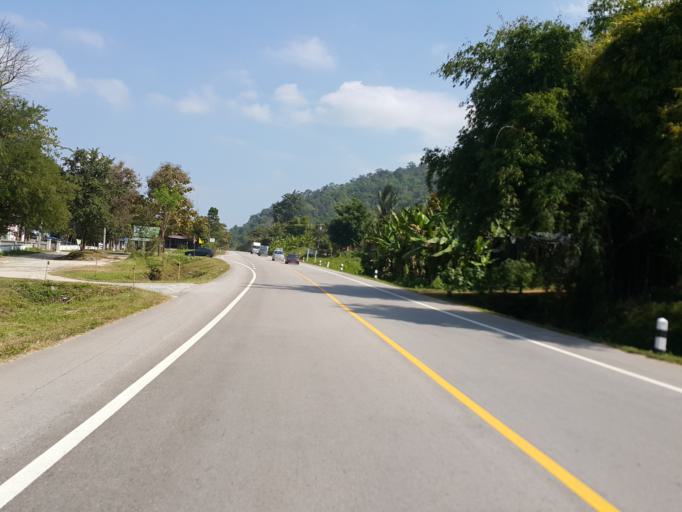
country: TH
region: Chiang Mai
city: Mae On
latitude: 19.0399
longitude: 99.3349
